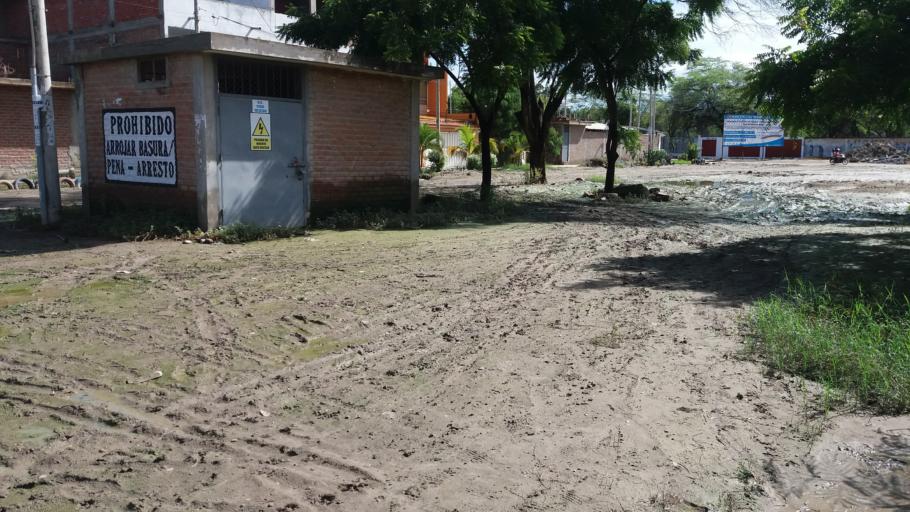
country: PE
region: Piura
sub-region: Provincia de Piura
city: Piura
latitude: -5.1770
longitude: -80.6406
